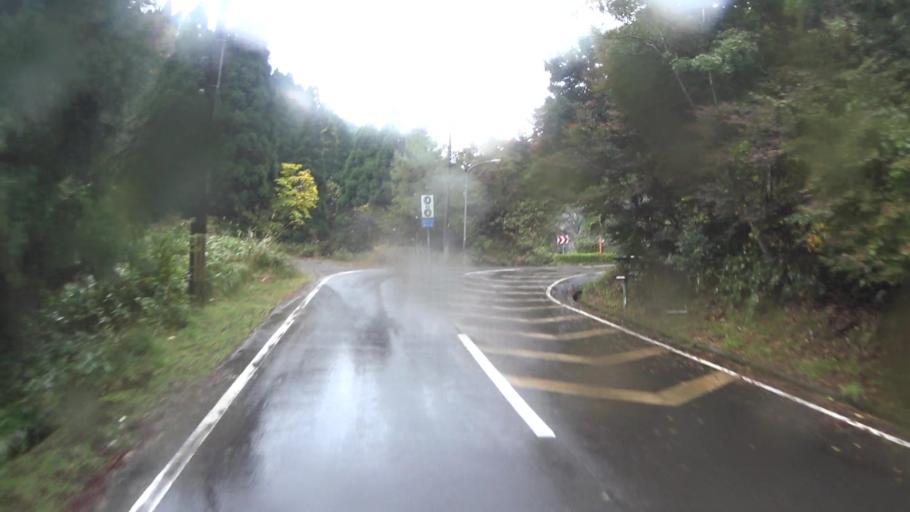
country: JP
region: Kyoto
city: Miyazu
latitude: 35.4699
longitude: 135.1483
